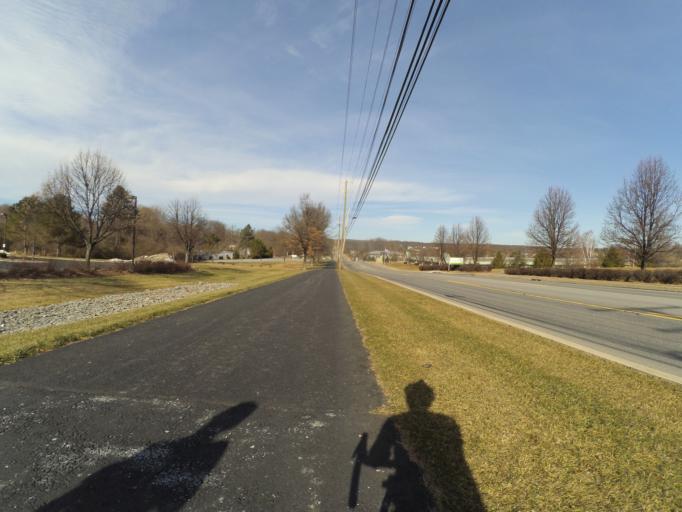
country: US
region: Pennsylvania
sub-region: Centre County
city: Park Forest Village
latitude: 40.7832
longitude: -77.9008
